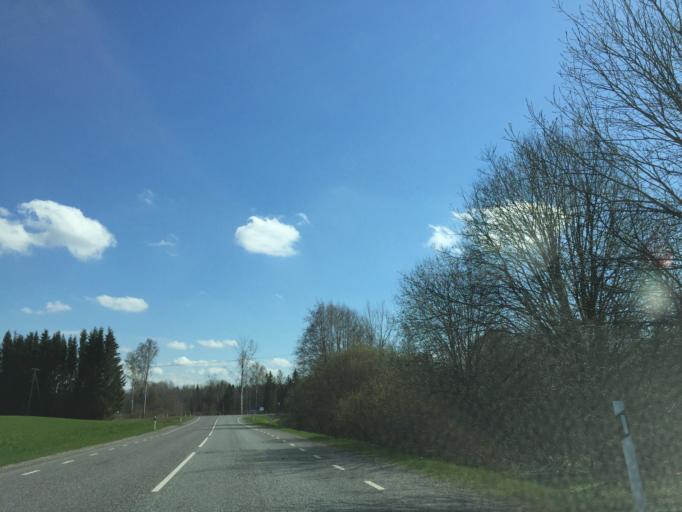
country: EE
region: Tartu
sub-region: Elva linn
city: Elva
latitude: 58.1476
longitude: 26.2293
